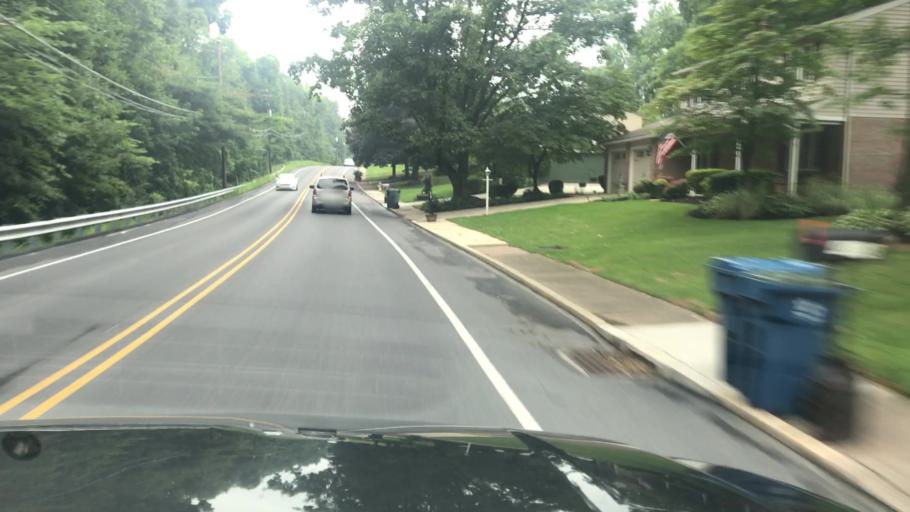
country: US
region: Pennsylvania
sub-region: Cumberland County
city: Shiremanstown
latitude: 40.2478
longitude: -76.9560
